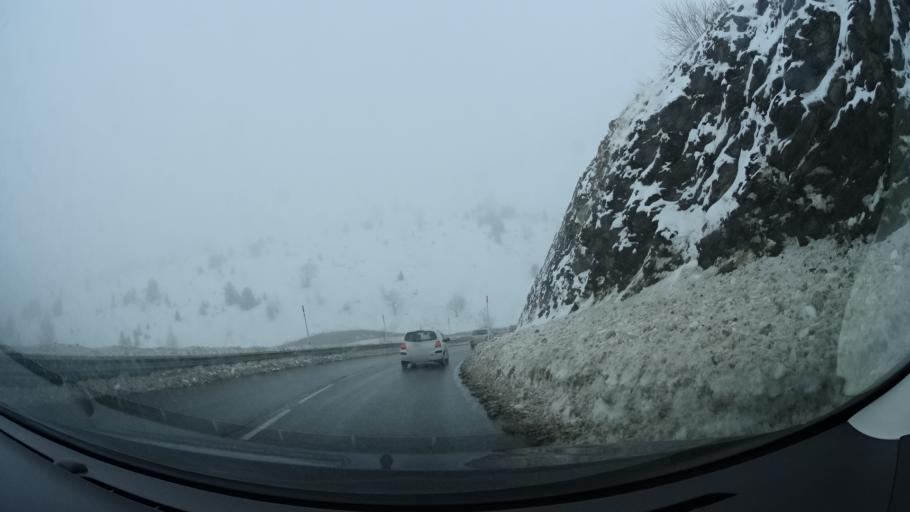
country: AD
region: Encamp
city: Pas de la Casa
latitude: 42.5612
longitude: 1.7772
